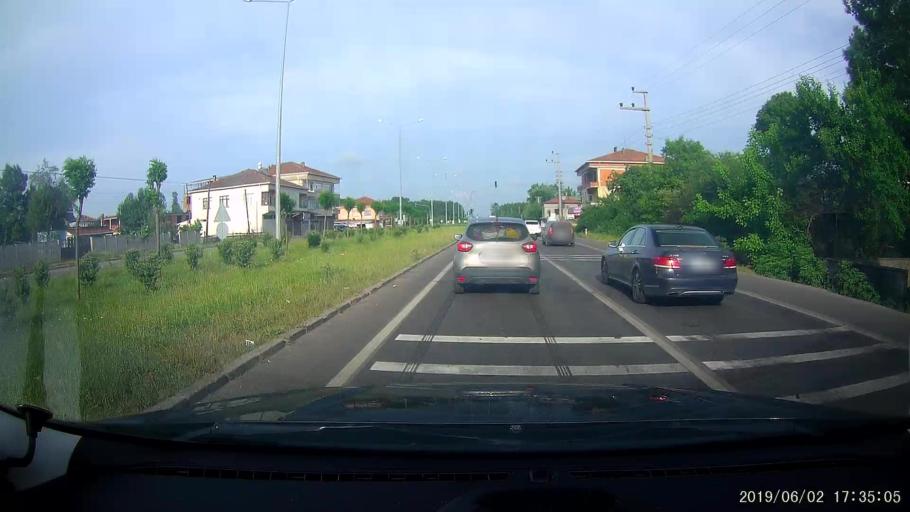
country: TR
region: Samsun
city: Terme
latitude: 41.2197
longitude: 36.8798
